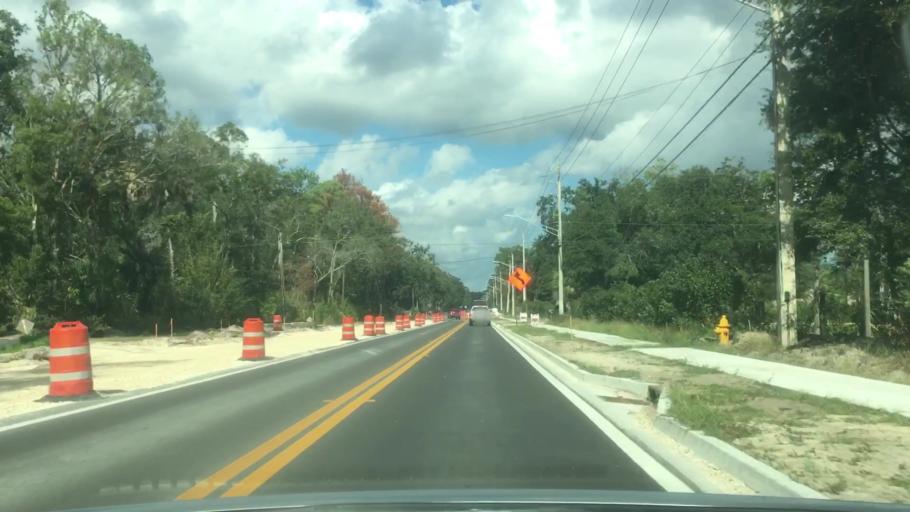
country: US
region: Florida
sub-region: Duval County
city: Atlantic Beach
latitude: 30.3437
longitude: -81.4614
